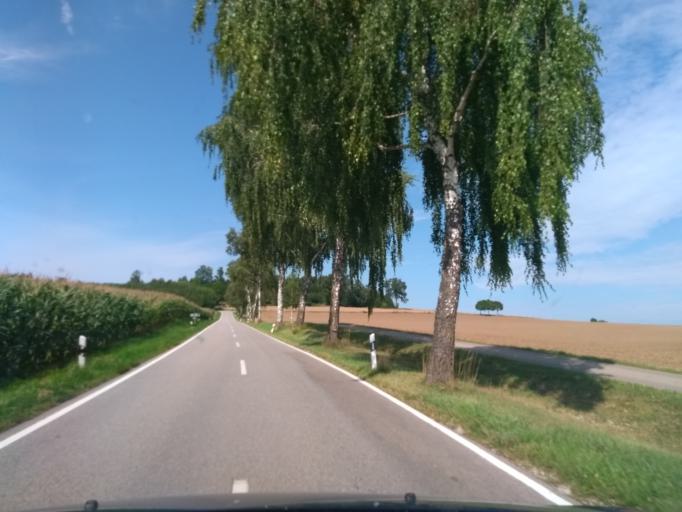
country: DE
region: Bavaria
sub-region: Upper Bavaria
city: Schwabhausen
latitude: 48.3970
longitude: 11.3483
